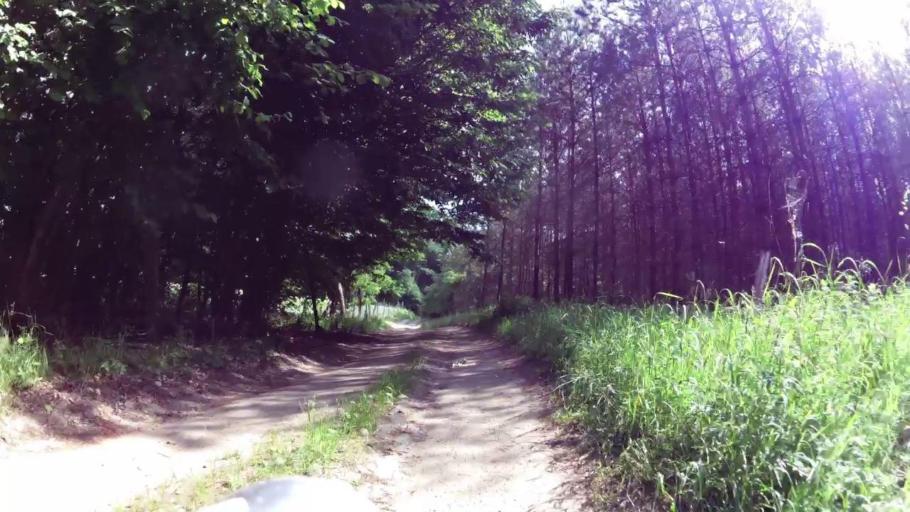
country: PL
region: West Pomeranian Voivodeship
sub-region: Powiat koszalinski
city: Bobolice
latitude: 53.9579
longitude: 16.6782
